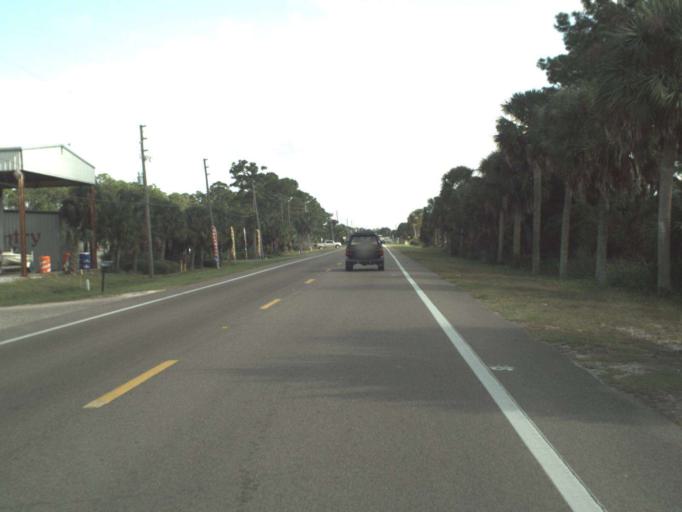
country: US
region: Florida
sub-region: Gulf County
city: Port Saint Joe
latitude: 29.8450
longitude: -85.3245
